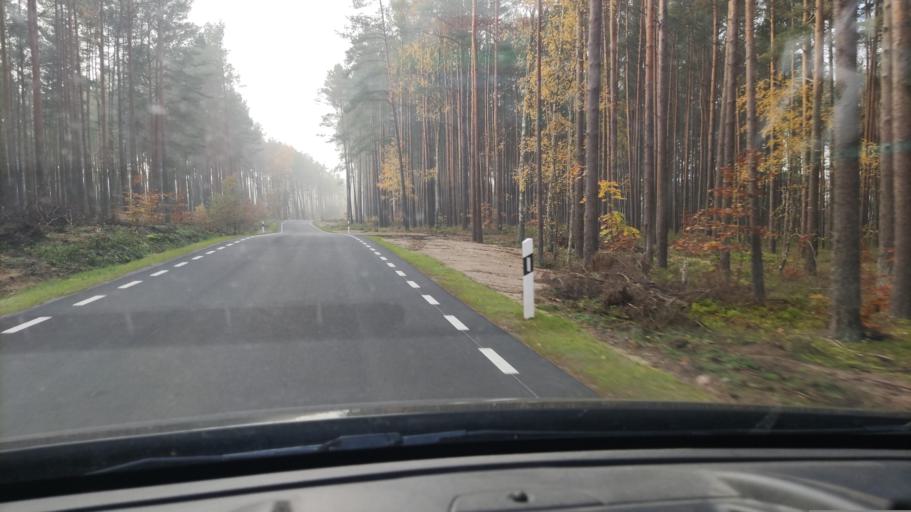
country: DE
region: Brandenburg
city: Furstenberg
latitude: 53.2417
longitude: 13.0891
